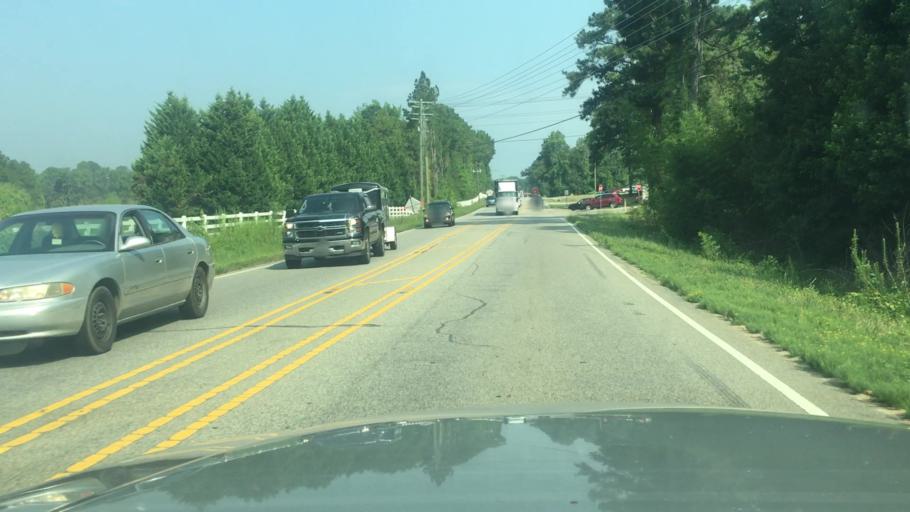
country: US
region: North Carolina
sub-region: Cumberland County
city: Hope Mills
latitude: 34.9291
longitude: -78.9136
